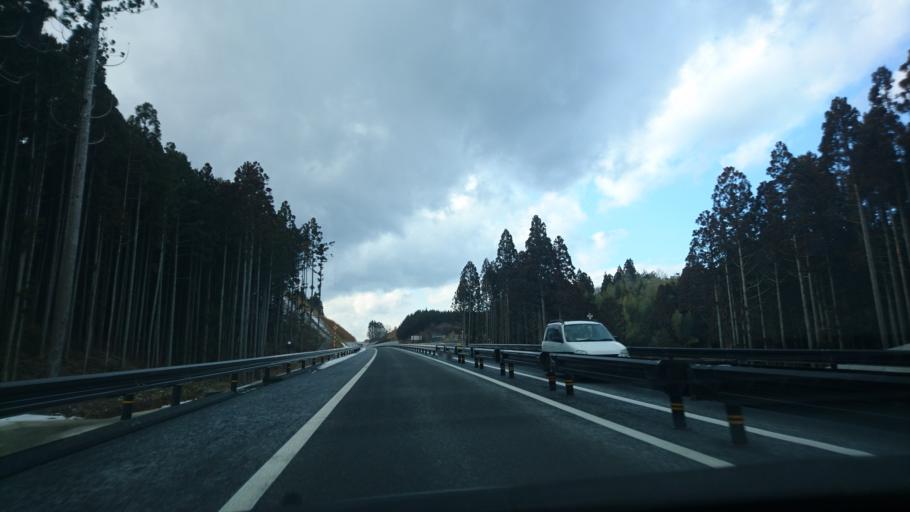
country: JP
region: Miyagi
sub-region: Oshika Gun
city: Onagawa Cho
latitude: 38.7550
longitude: 141.5114
